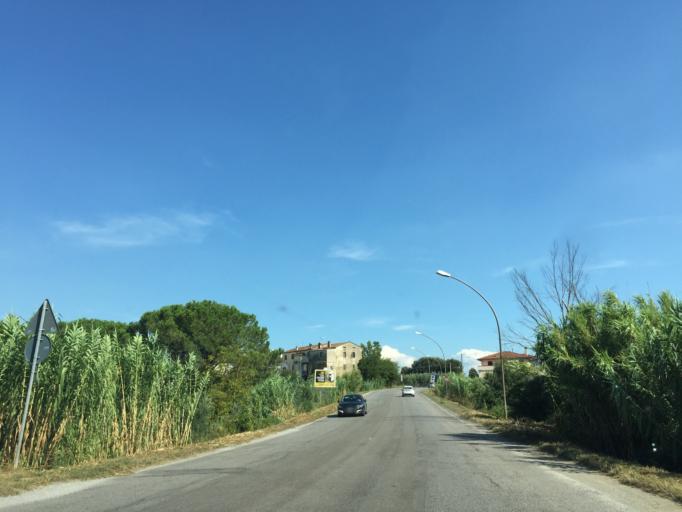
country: IT
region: Tuscany
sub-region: Provincia di Pistoia
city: San Rocco
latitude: 43.8238
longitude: 10.8697
